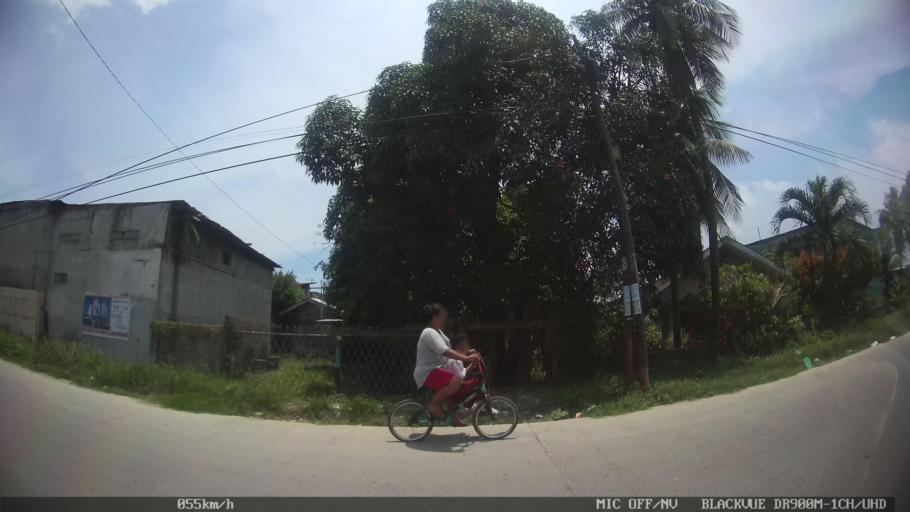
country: ID
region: North Sumatra
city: Labuhan Deli
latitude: 3.7198
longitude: 98.6804
